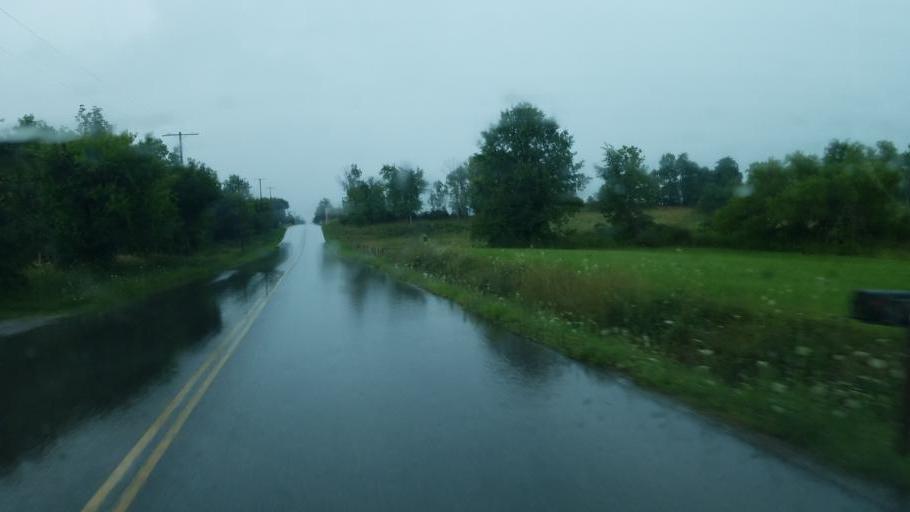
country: US
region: Ohio
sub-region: Geauga County
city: Middlefield
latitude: 41.5087
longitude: -80.9800
